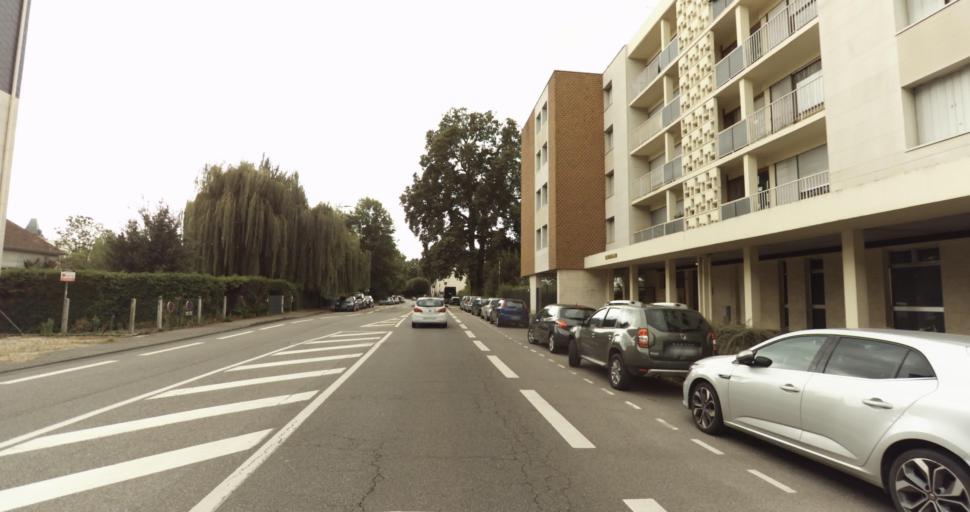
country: FR
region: Haute-Normandie
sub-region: Departement de l'Eure
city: Evreux
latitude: 49.0259
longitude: 1.1384
